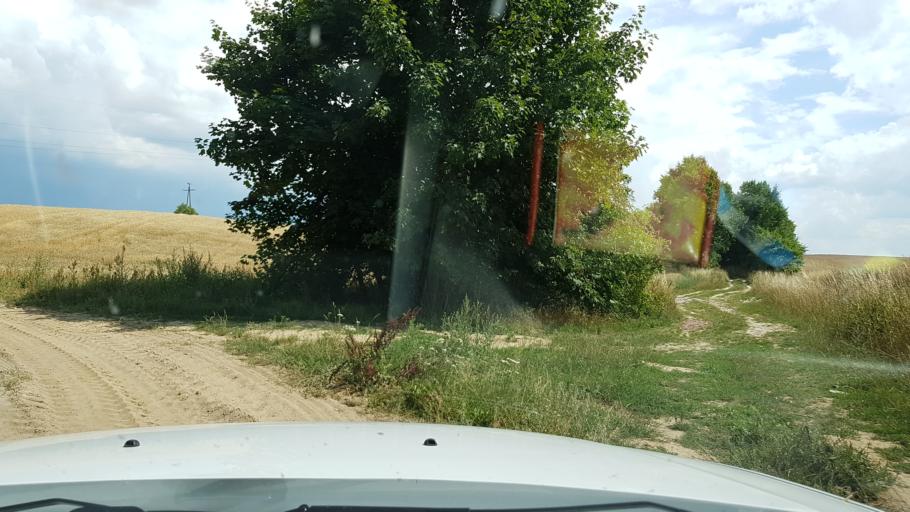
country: PL
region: West Pomeranian Voivodeship
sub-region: Powiat walecki
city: Walcz
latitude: 53.2502
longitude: 16.5126
